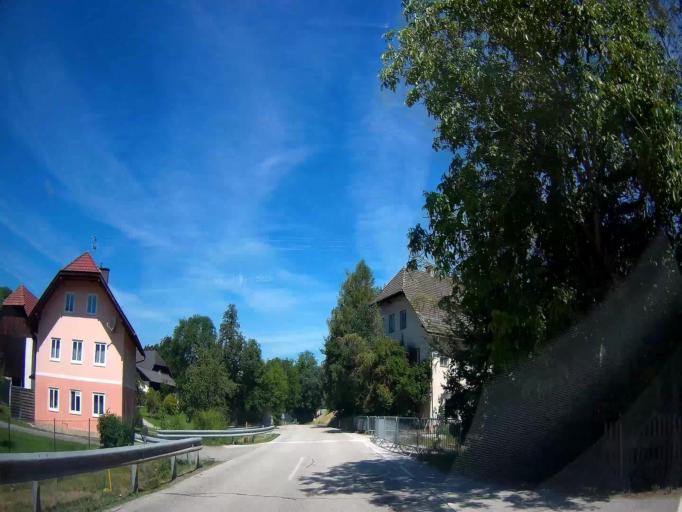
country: AT
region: Carinthia
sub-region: Politischer Bezirk Sankt Veit an der Glan
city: St. Georgen am Laengsee
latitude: 46.8010
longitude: 14.4130
